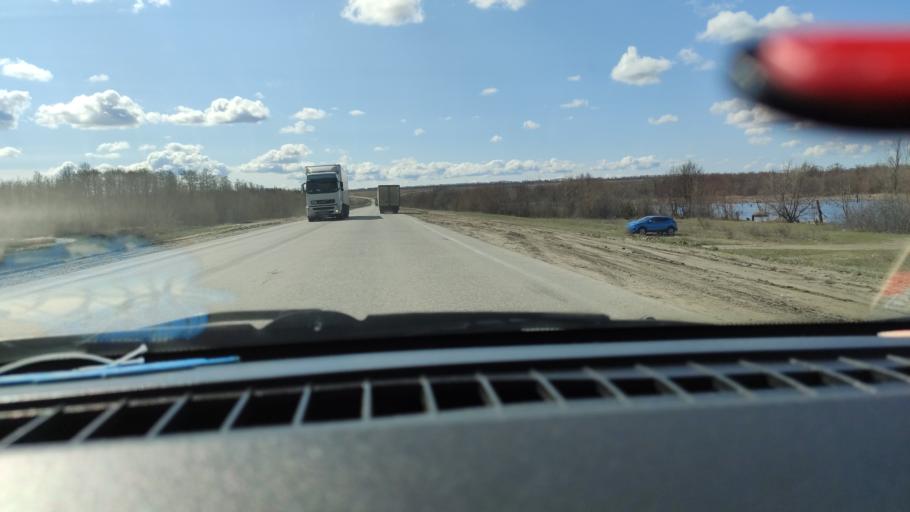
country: RU
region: Samara
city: Varlamovo
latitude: 53.1354
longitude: 48.2863
